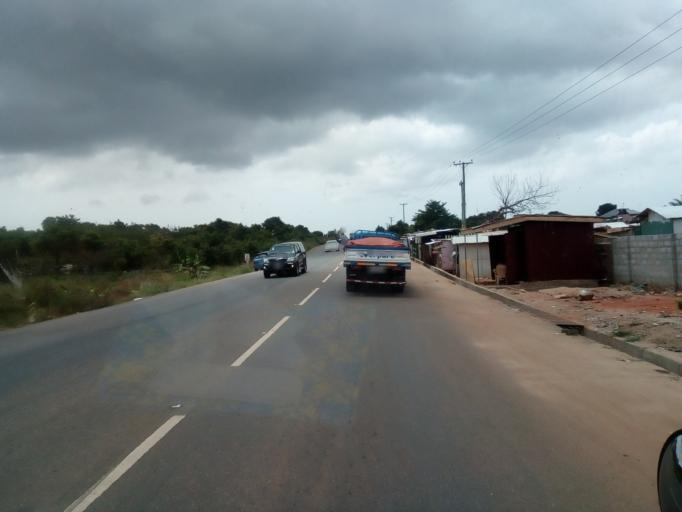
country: GH
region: Greater Accra
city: Dome
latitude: 5.6569
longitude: -0.2053
